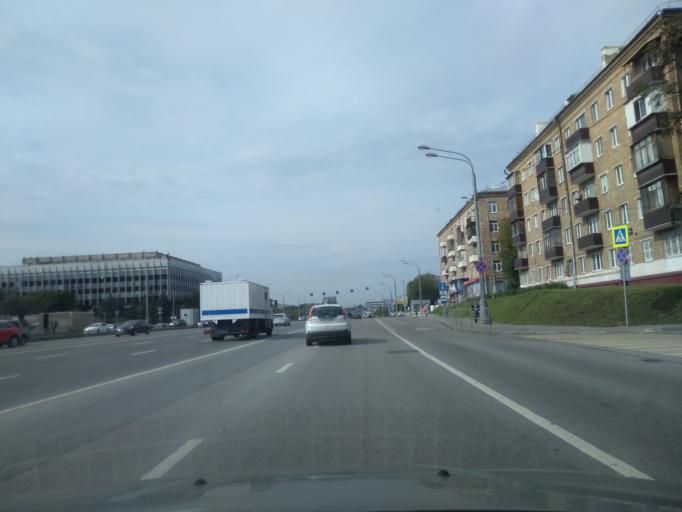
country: RU
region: Moscow
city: Strogino
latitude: 55.8261
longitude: 37.4275
